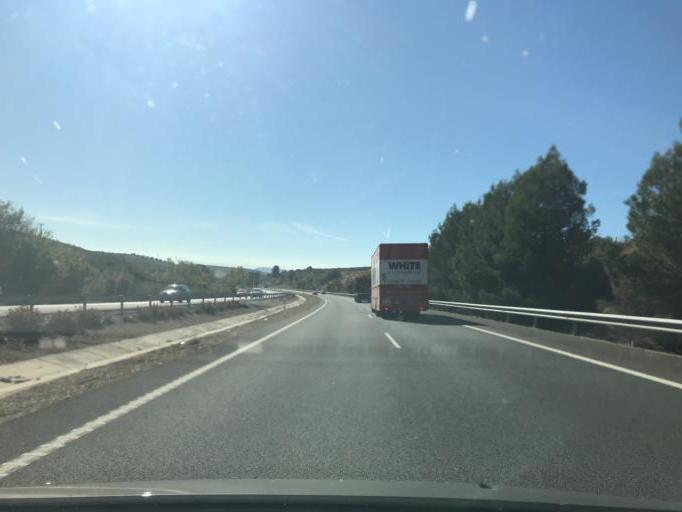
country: ES
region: Andalusia
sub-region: Provincia de Granada
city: Deifontes
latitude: 37.3600
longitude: -3.6103
